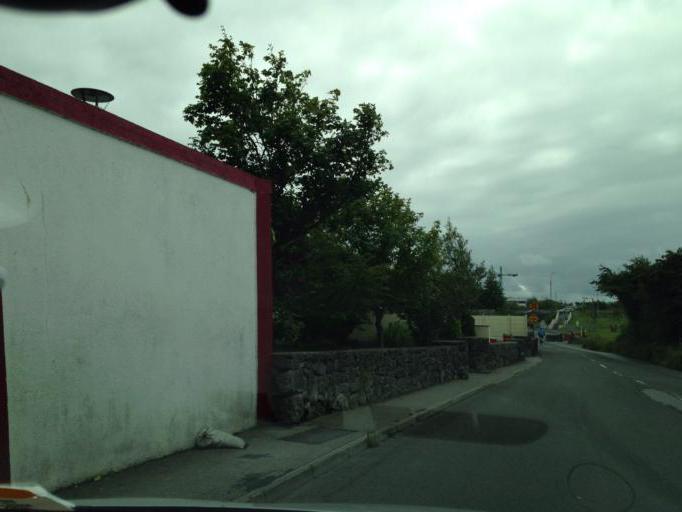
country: IE
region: Connaught
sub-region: County Galway
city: Gaillimh
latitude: 53.2847
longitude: -9.0575
